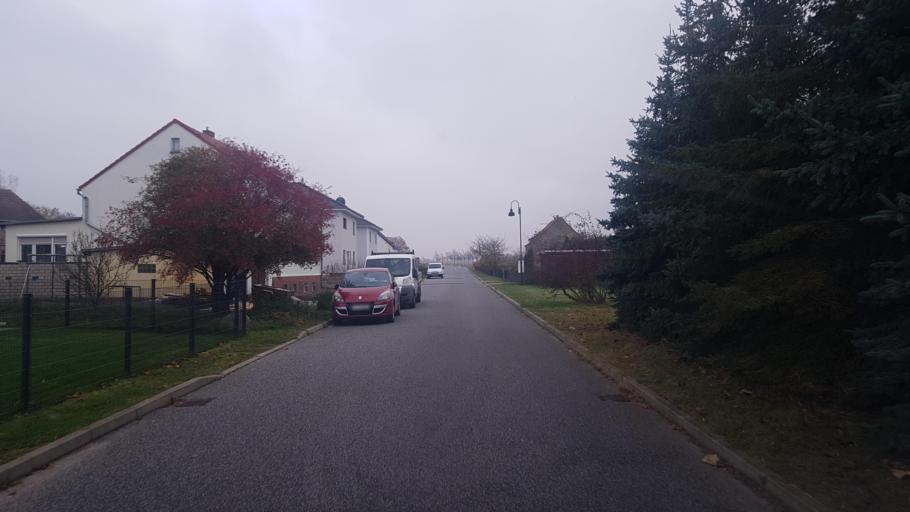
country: DE
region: Brandenburg
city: Gross Kreutz
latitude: 52.3985
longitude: 12.7799
